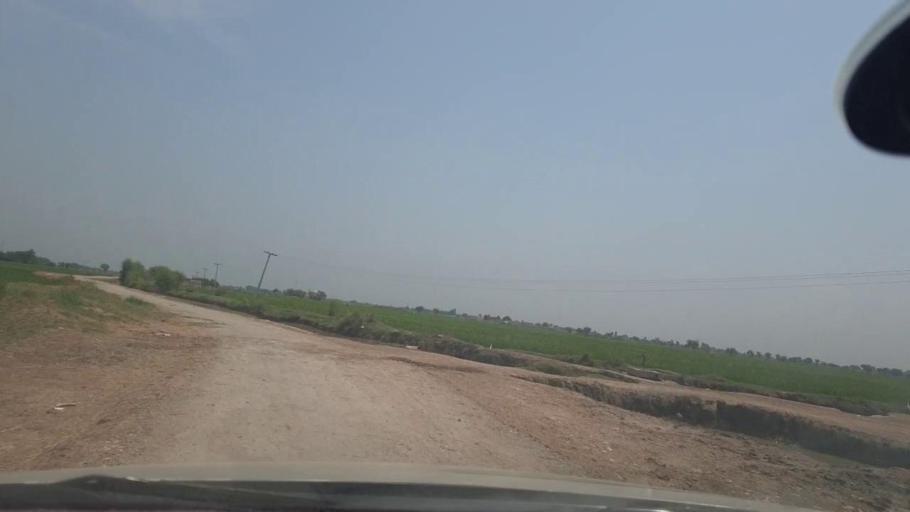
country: PK
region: Sindh
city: Jacobabad
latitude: 28.1681
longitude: 68.3927
